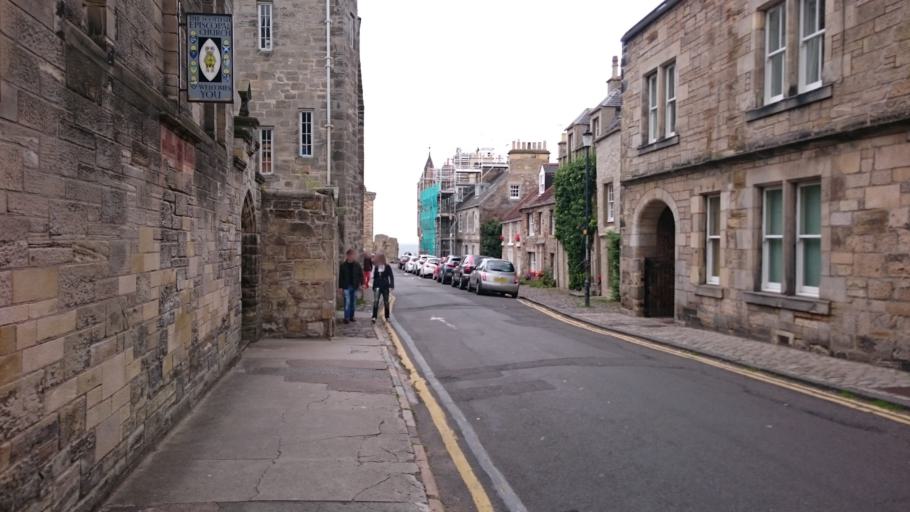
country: GB
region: Scotland
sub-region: Fife
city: Saint Andrews
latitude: 56.3409
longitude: -2.7907
